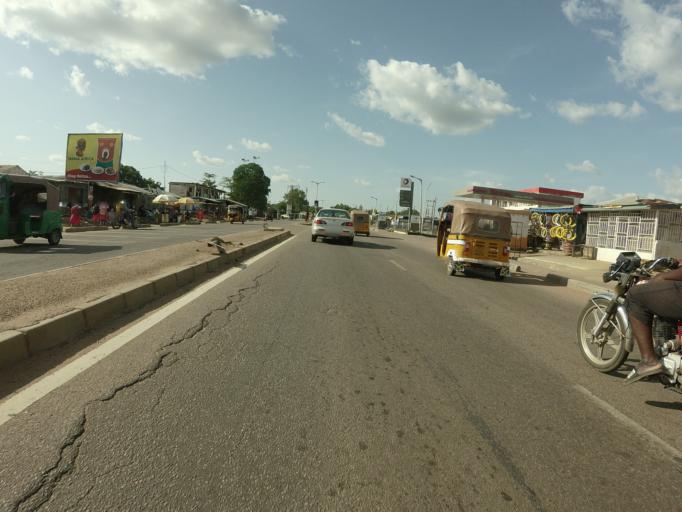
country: GH
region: Upper East
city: Bolgatanga
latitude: 10.7795
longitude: -0.8541
